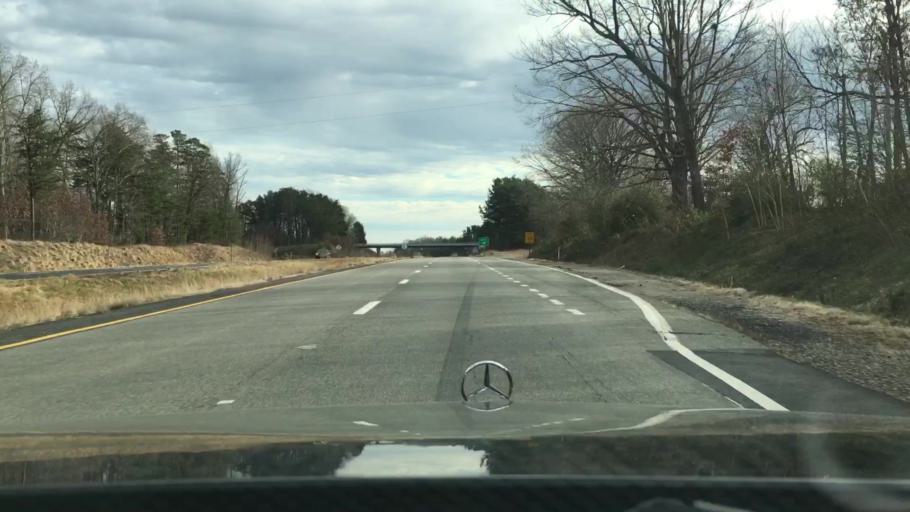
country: US
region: Virginia
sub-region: Pittsylvania County
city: Chatham
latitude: 36.8521
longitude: -79.3956
